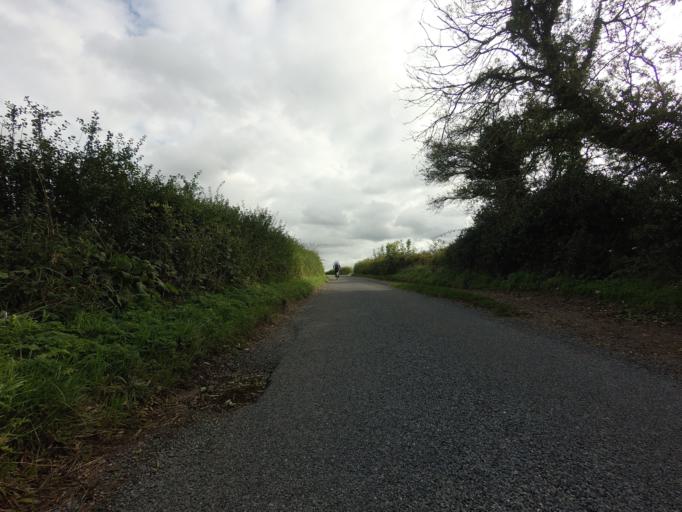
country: GB
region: England
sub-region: Norfolk
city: Dersingham
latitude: 52.8597
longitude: 0.5132
